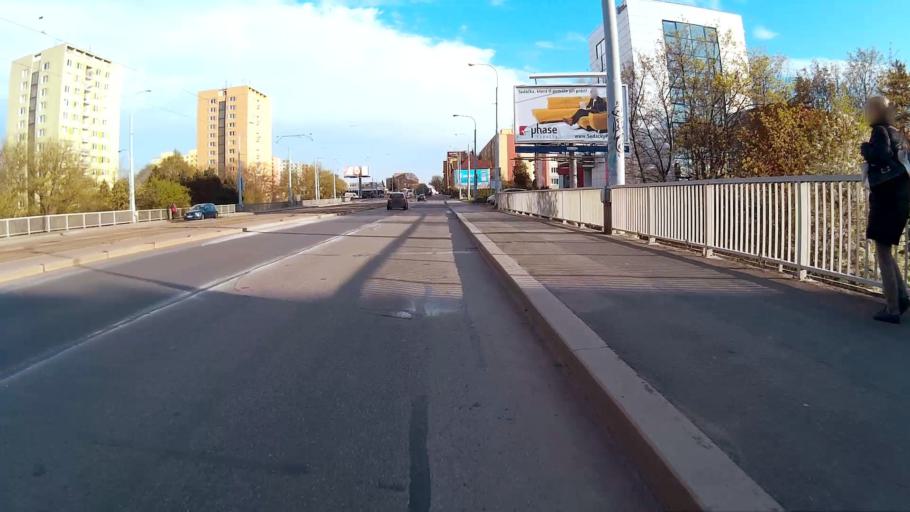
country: CZ
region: South Moravian
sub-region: Mesto Brno
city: Mokra Hora
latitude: 49.2335
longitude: 16.5884
